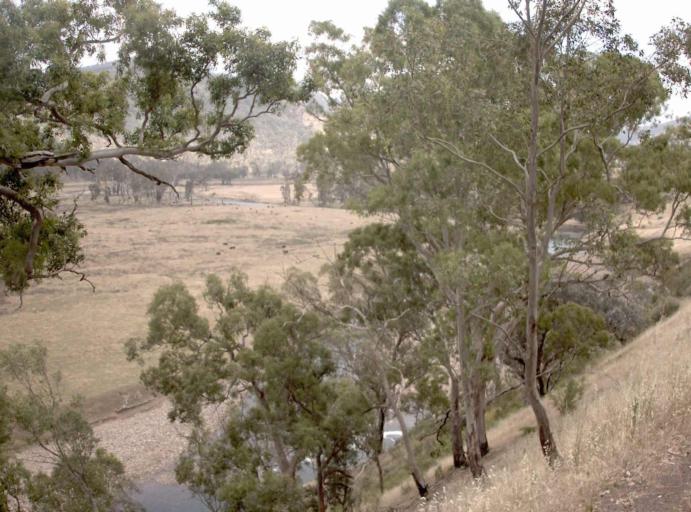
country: AU
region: Victoria
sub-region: Wellington
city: Heyfield
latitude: -37.6634
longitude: 146.6460
